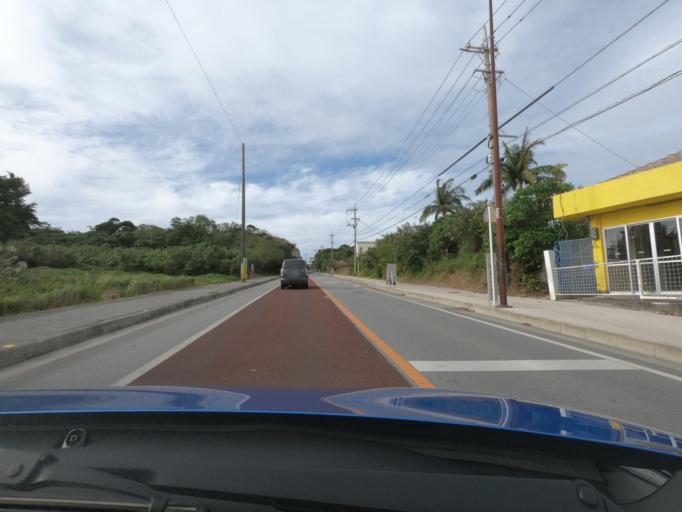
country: JP
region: Okinawa
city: Nago
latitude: 26.6791
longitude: 127.8877
